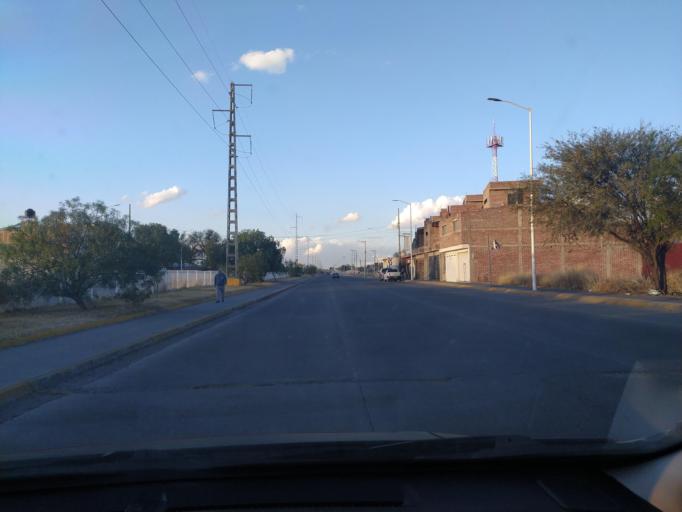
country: LA
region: Oudomxai
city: Muang La
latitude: 21.0086
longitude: 101.8700
